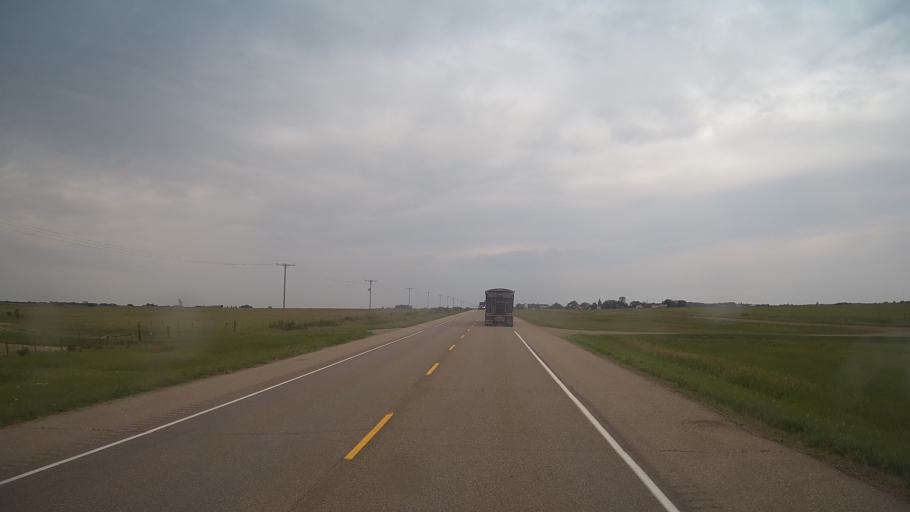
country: CA
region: Saskatchewan
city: Langham
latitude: 52.1289
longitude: -107.1810
